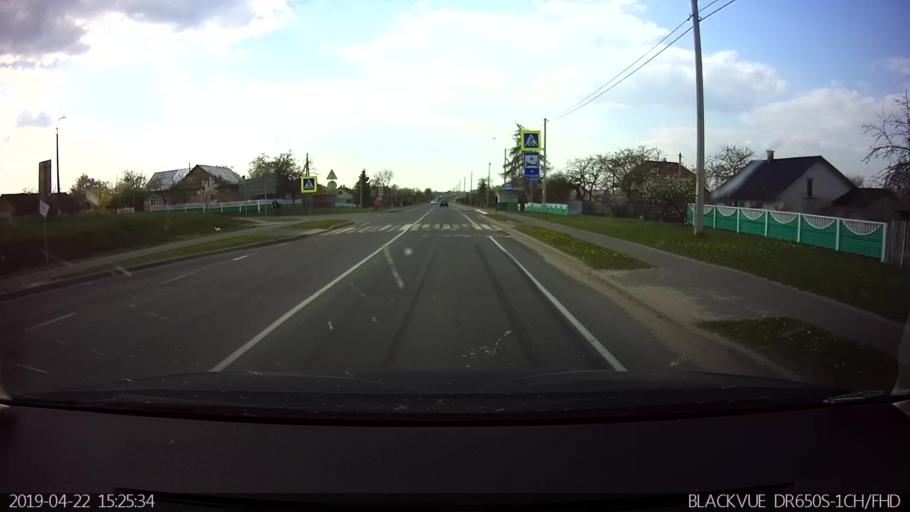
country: BY
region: Brest
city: Vysokaye
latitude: 52.3649
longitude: 23.3942
